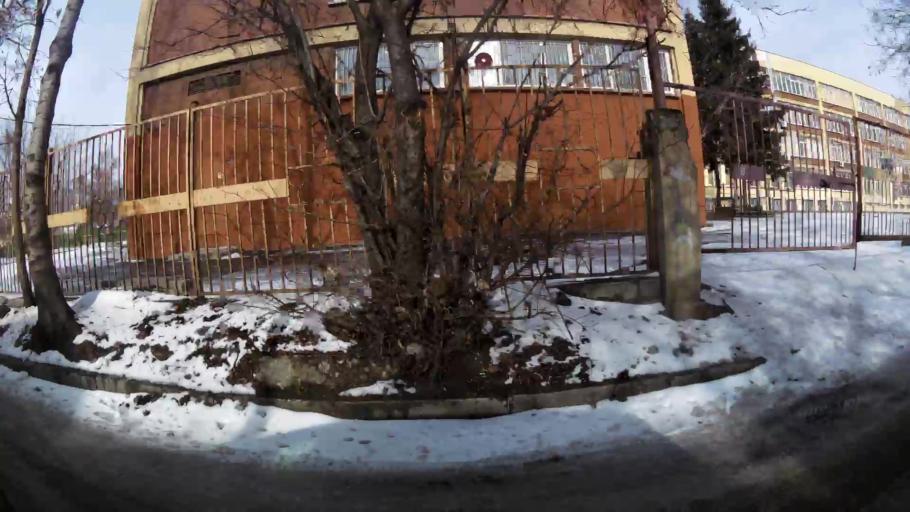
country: BG
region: Sofia-Capital
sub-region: Stolichna Obshtina
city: Sofia
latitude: 42.7068
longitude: 23.3585
